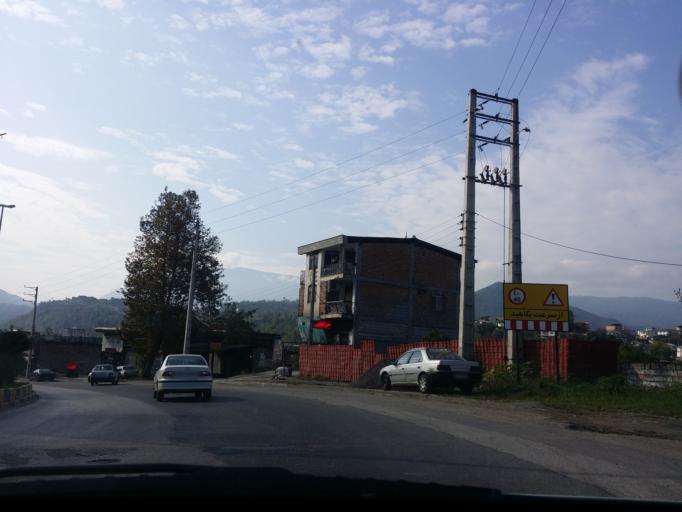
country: IR
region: Mazandaran
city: Chalus
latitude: 36.6491
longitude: 51.4143
